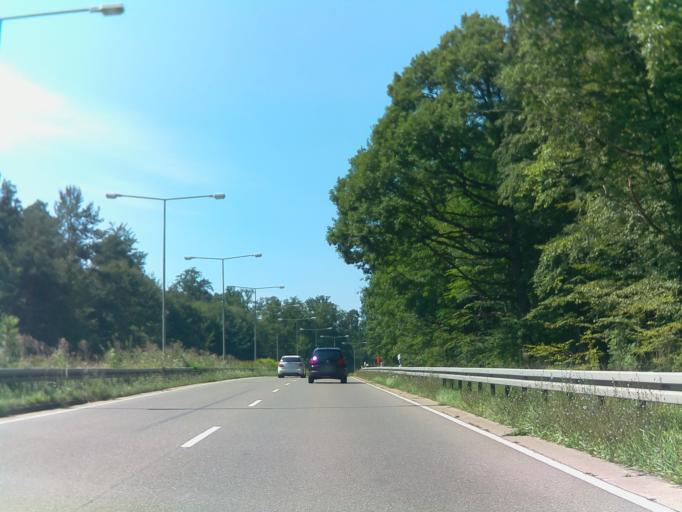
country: DE
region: Baden-Wuerttemberg
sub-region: Regierungsbezirk Stuttgart
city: Gerlingen
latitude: 48.7841
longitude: 9.0770
